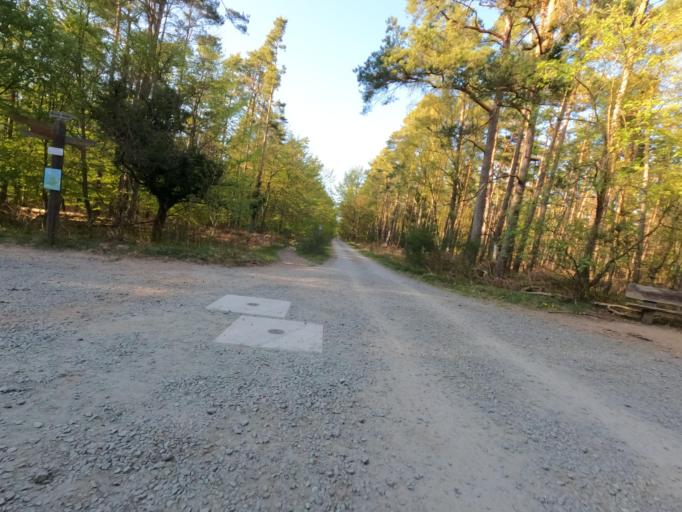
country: DE
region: Mecklenburg-Vorpommern
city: Born
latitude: 54.4158
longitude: 12.5329
